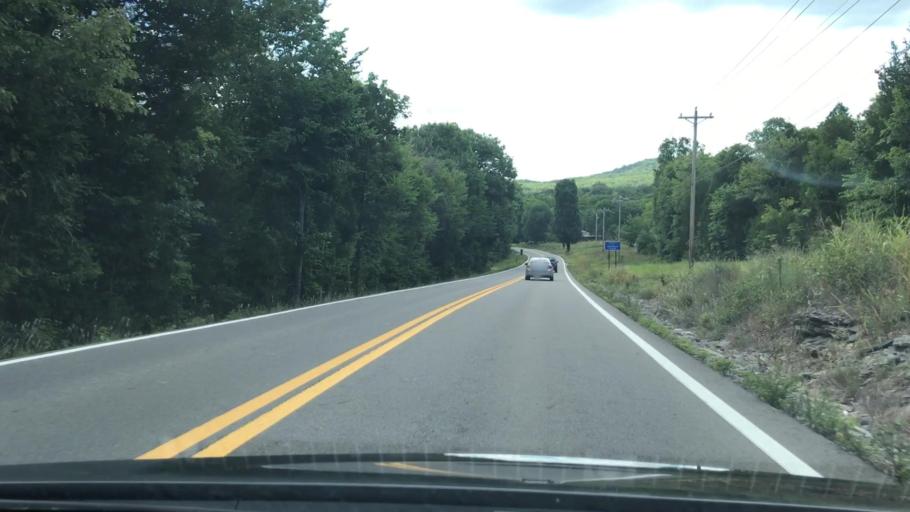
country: US
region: Tennessee
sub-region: Williamson County
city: Nolensville
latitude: 35.8515
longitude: -86.6001
